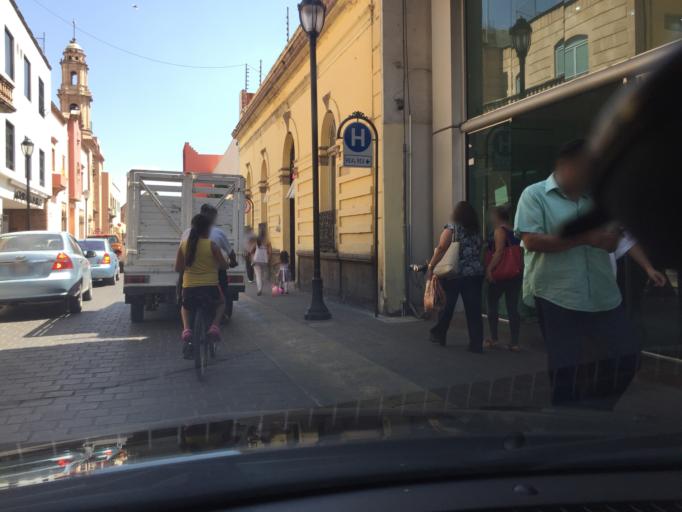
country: MX
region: Guanajuato
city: Leon
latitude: 21.1210
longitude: -101.6821
